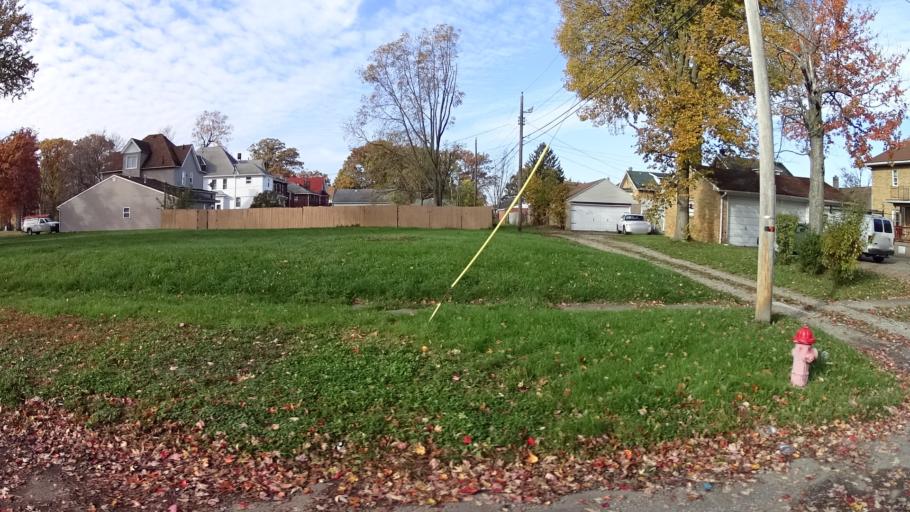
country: US
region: Ohio
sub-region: Lorain County
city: Sheffield
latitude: 41.4431
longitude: -82.1239
